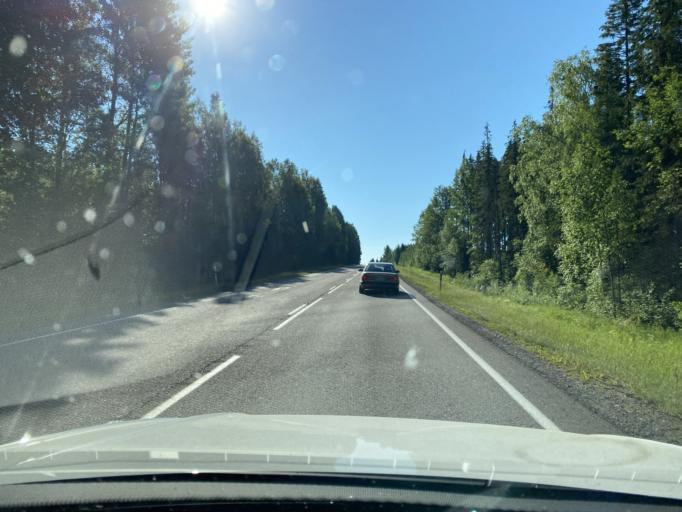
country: FI
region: Haeme
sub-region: Haemeenlinna
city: Renko
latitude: 60.7743
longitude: 24.1983
